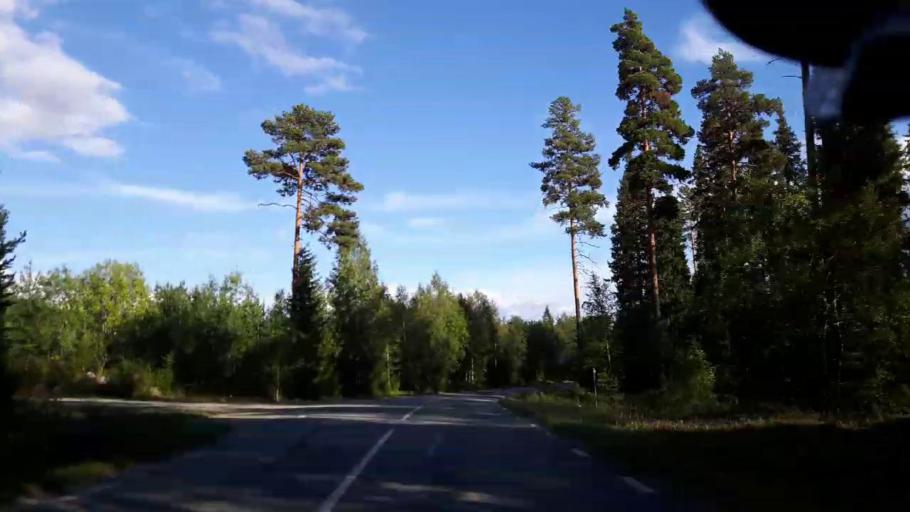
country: SE
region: Jaemtland
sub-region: Stroemsunds Kommun
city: Stroemsund
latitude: 63.3744
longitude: 15.5631
